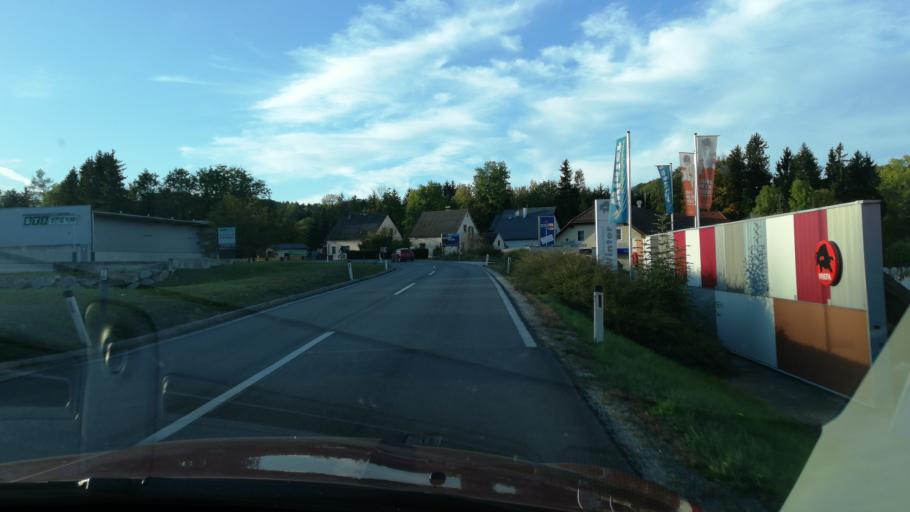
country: AT
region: Upper Austria
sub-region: Politischer Bezirk Steyr-Land
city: Waldneukirchen
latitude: 47.9915
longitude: 14.2742
